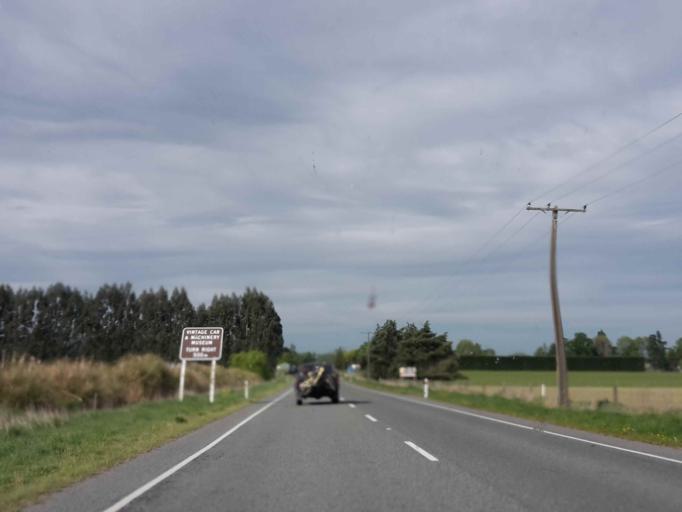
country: NZ
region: Canterbury
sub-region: Timaru District
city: Pleasant Point
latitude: -44.1100
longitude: 171.2302
